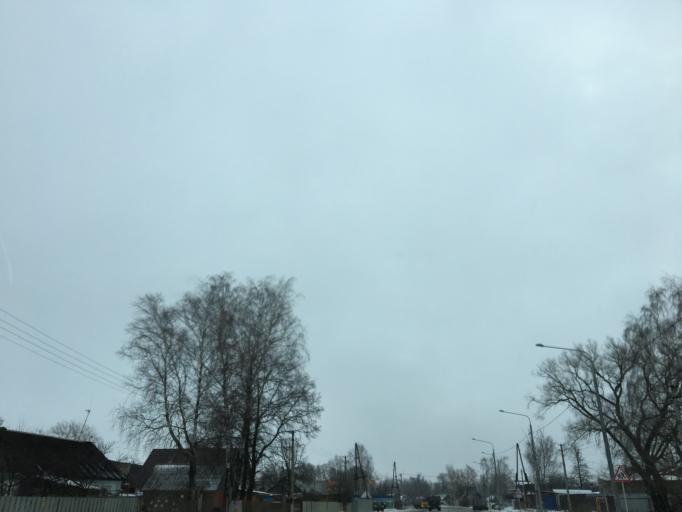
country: RU
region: Tula
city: Bolokhovo
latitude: 54.0506
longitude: 37.8217
